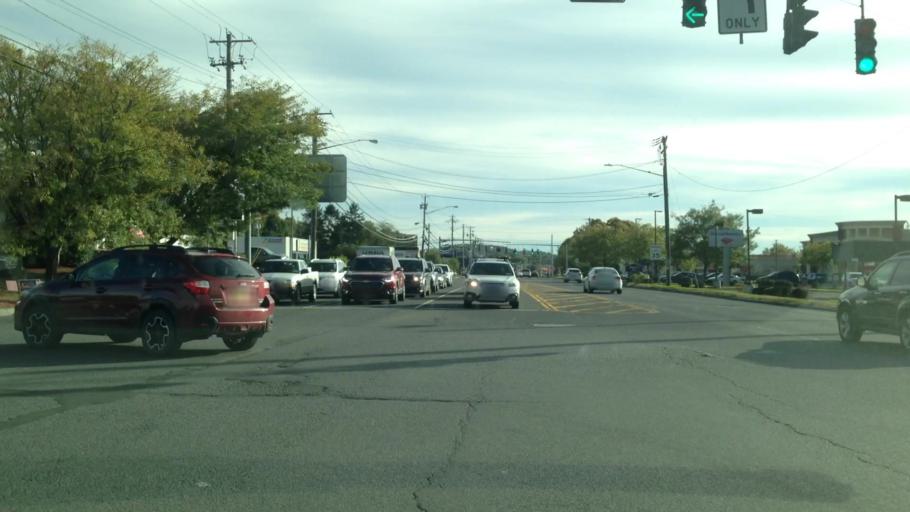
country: US
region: New York
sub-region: Ulster County
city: Lake Katrine
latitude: 41.9711
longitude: -73.9888
